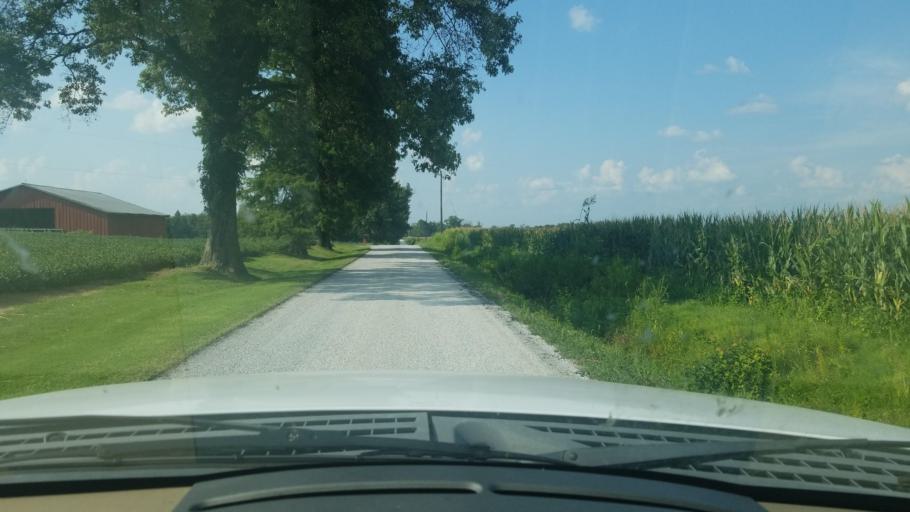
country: US
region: Illinois
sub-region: Saline County
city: Eldorado
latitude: 37.8422
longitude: -88.4802
